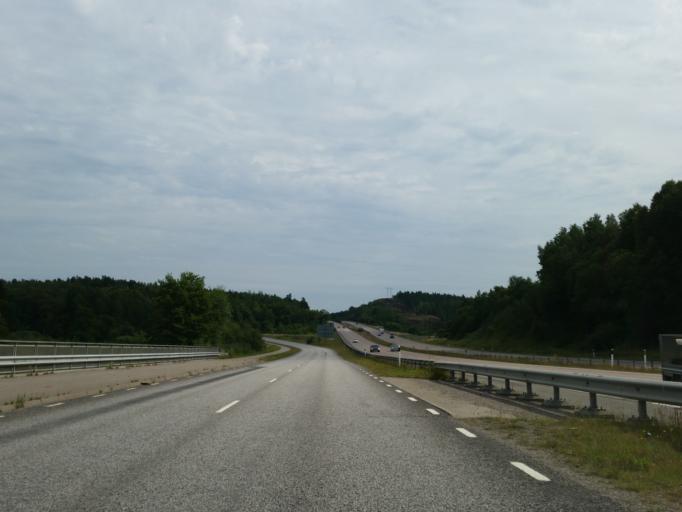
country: SE
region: Soedermanland
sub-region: Strangnas Kommun
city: Mariefred
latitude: 59.2441
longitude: 17.1725
